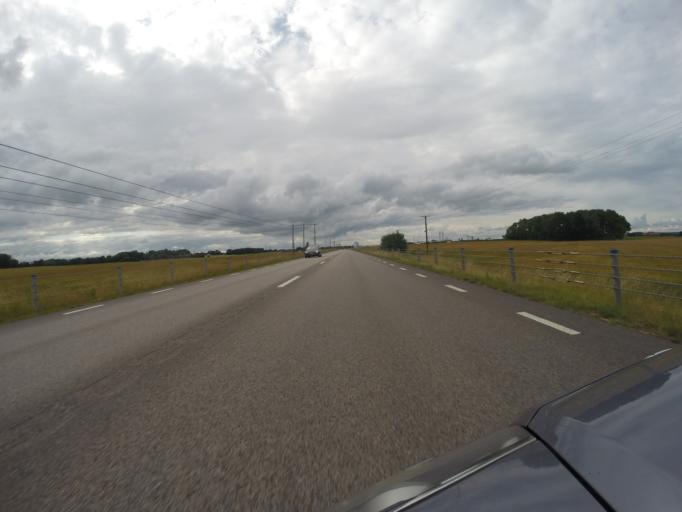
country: SE
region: Skane
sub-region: Bjuvs Kommun
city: Bjuv
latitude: 56.0627
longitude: 12.9498
